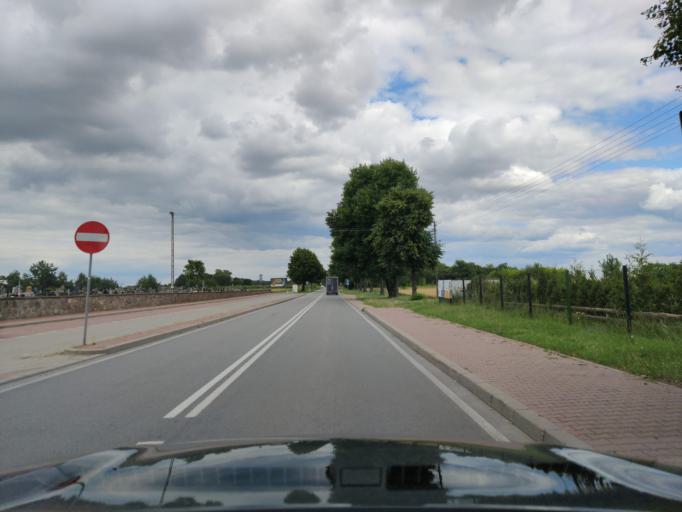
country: PL
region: Masovian Voivodeship
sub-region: Powiat sokolowski
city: Kosow Lacki
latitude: 52.5966
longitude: 22.1580
